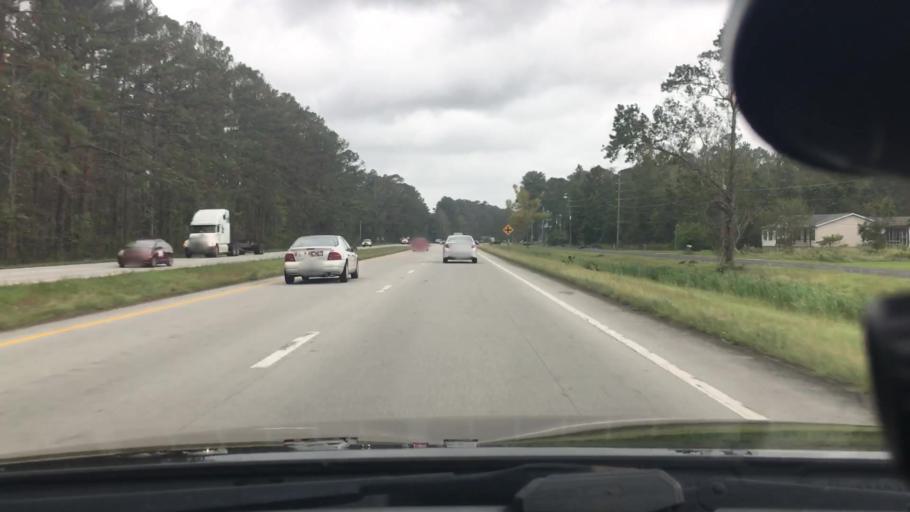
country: US
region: North Carolina
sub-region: Craven County
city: Neuse Forest
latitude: 34.9862
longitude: -76.9805
